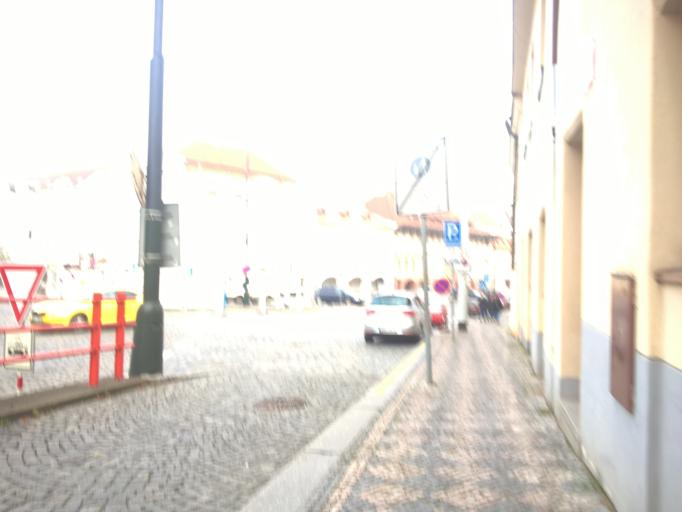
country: CZ
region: Praha
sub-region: Praha 1
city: Mala Strana
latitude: 50.0870
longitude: 14.3881
